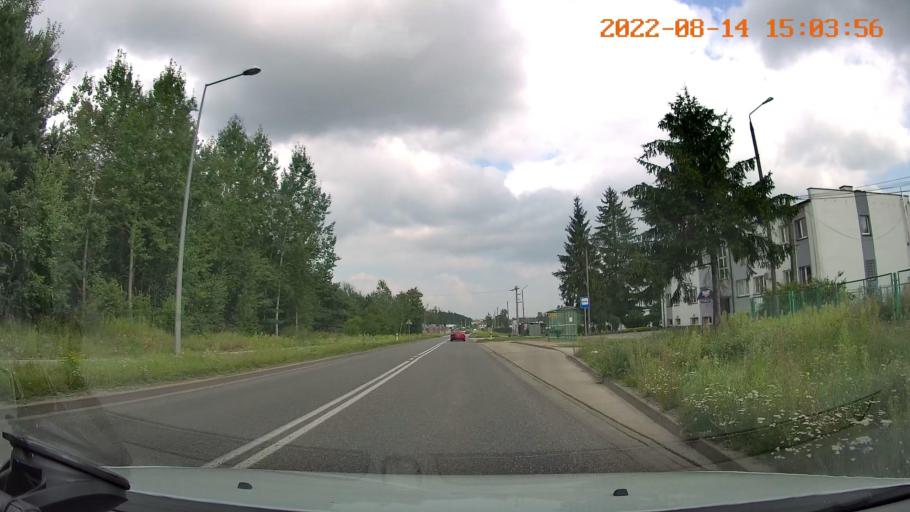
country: PL
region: Swietokrzyskie
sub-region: Powiat kielecki
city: Kostomloty Drugie
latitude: 50.8822
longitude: 20.5413
